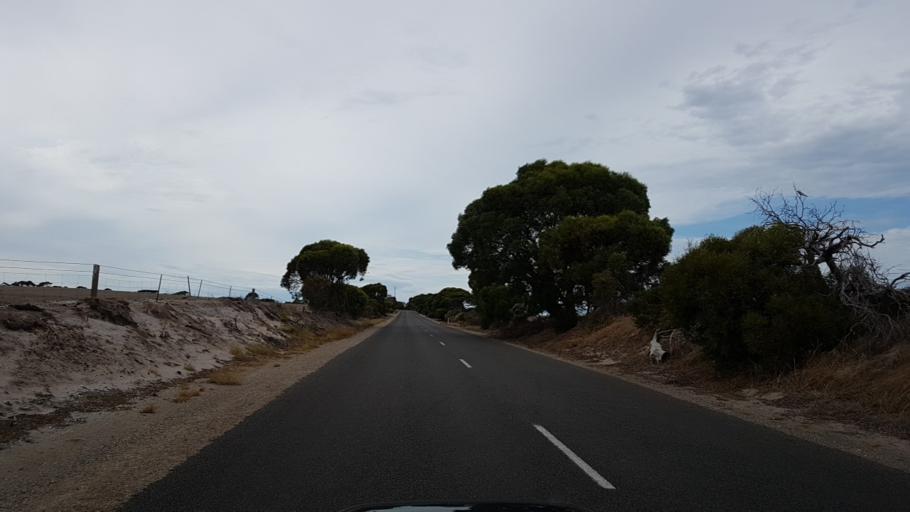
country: AU
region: South Australia
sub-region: Yorke Peninsula
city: Honiton
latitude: -34.9843
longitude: 137.1232
